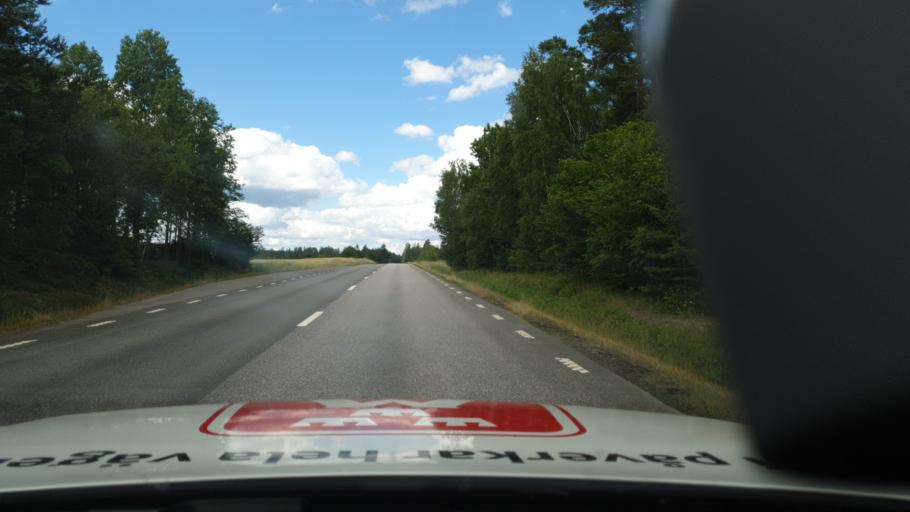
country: SE
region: Vaestra Goetaland
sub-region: Karlsborgs Kommun
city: Molltorp
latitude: 58.4541
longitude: 14.4034
